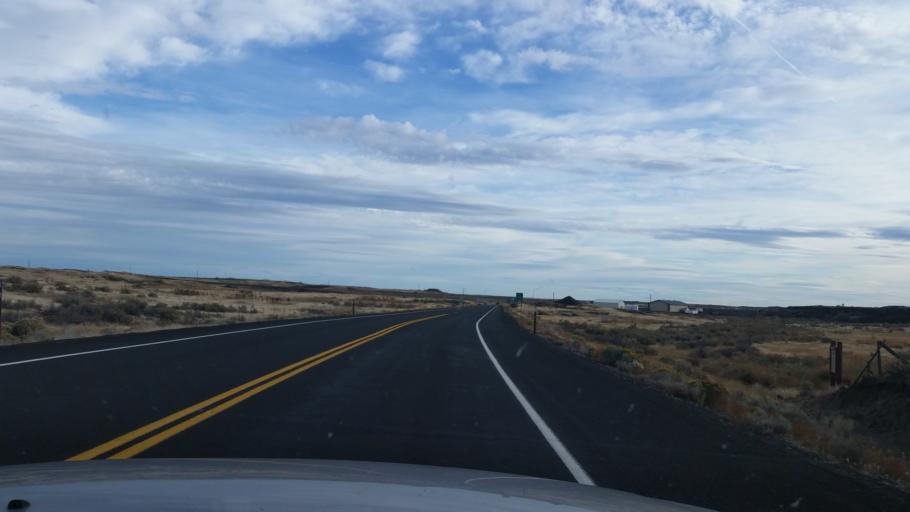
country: US
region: Washington
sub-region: Lincoln County
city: Davenport
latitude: 47.3150
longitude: -117.9738
